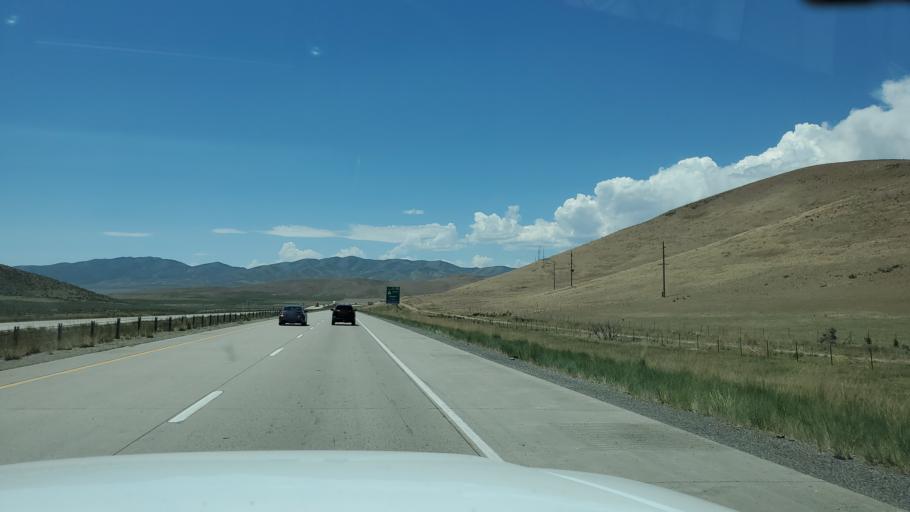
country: US
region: Utah
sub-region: Box Elder County
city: Garland
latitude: 41.8157
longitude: -112.3910
